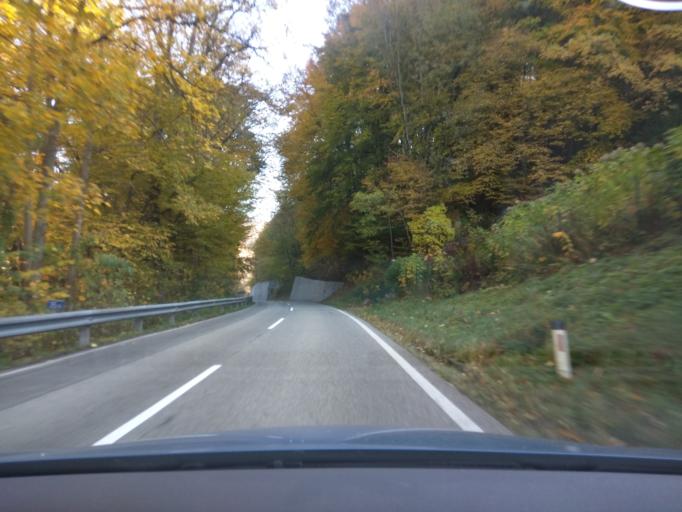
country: DE
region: Bavaria
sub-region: Lower Bavaria
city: Untergriesbach
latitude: 48.5145
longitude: 13.7127
